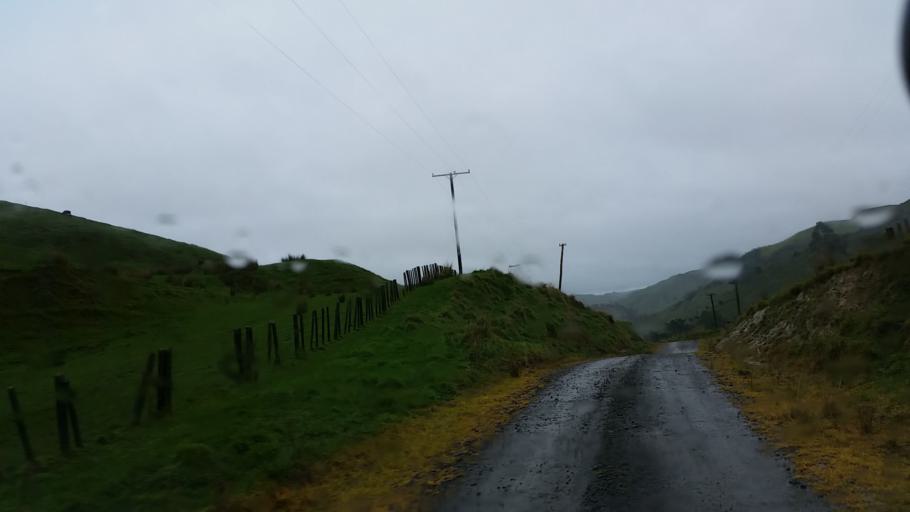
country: NZ
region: Taranaki
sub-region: South Taranaki District
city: Eltham
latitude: -39.4760
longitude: 174.4118
